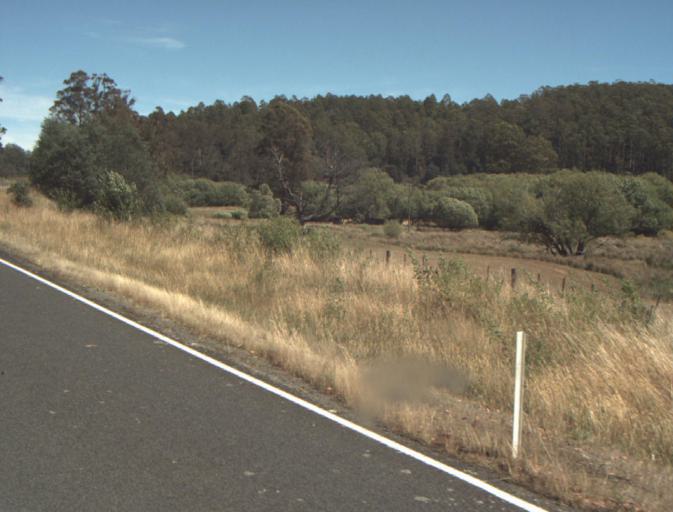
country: AU
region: Tasmania
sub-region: Dorset
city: Scottsdale
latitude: -41.2984
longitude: 147.3842
